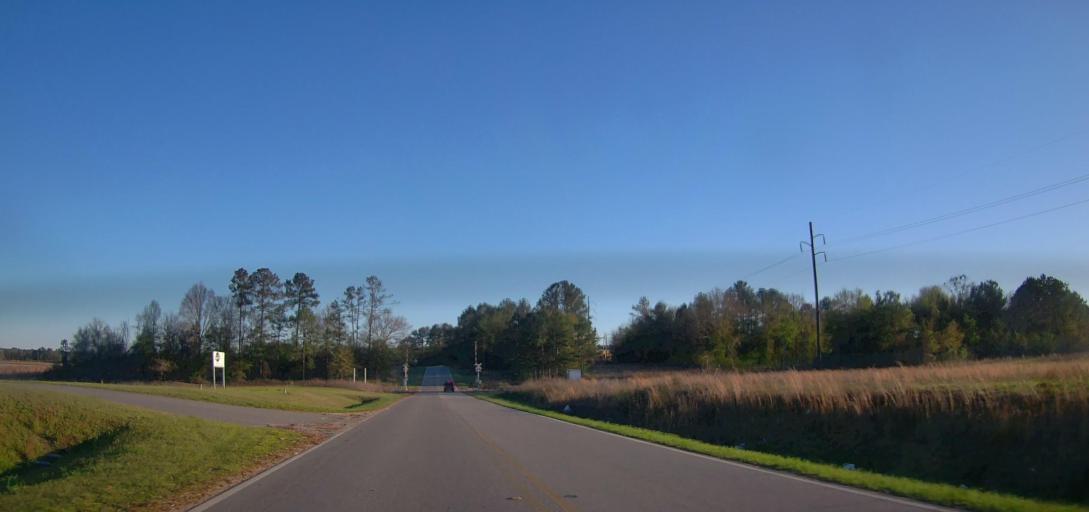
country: US
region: Georgia
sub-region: Wilkinson County
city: Gordon
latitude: 32.8949
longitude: -83.3013
